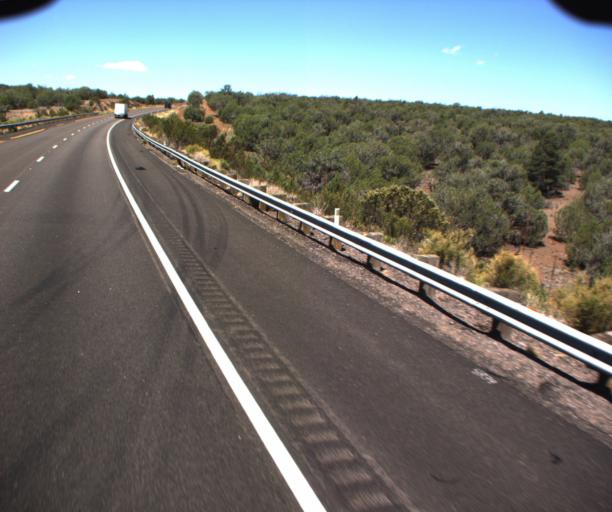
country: US
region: Arizona
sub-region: Mohave County
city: Peach Springs
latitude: 35.1899
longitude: -113.3186
